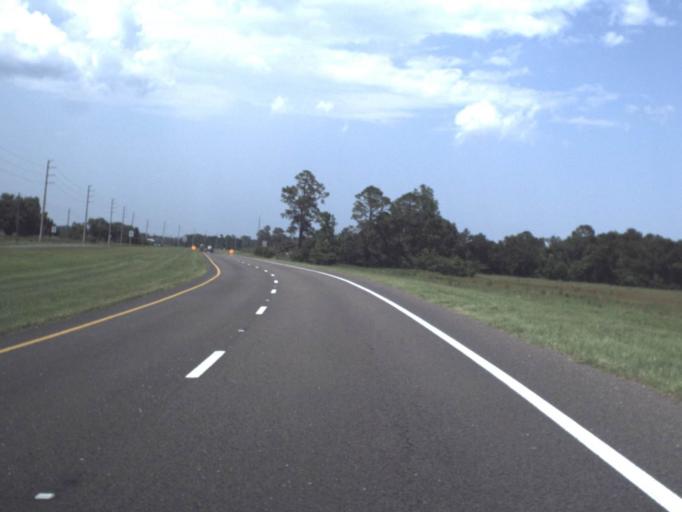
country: US
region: Florida
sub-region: Putnam County
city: East Palatka
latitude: 29.7452
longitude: -81.4711
